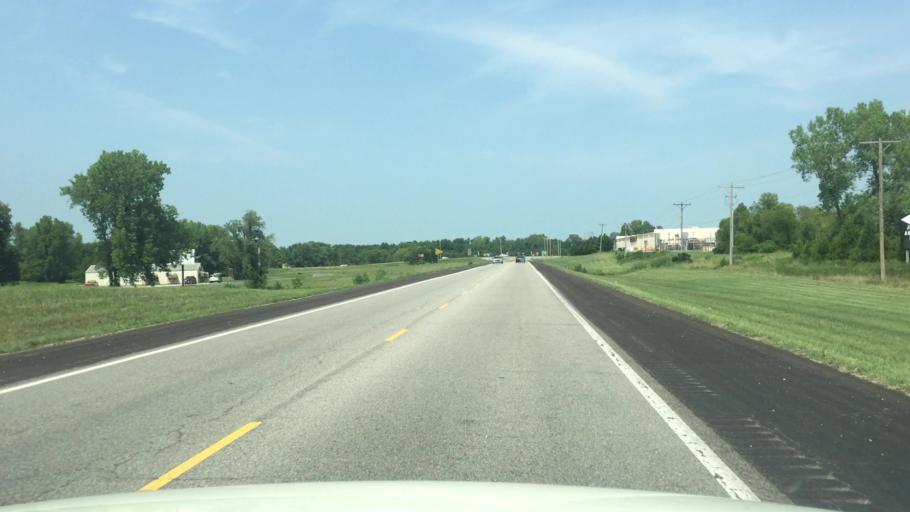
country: US
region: Kansas
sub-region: Crawford County
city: Pittsburg
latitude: 37.4356
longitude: -94.7100
